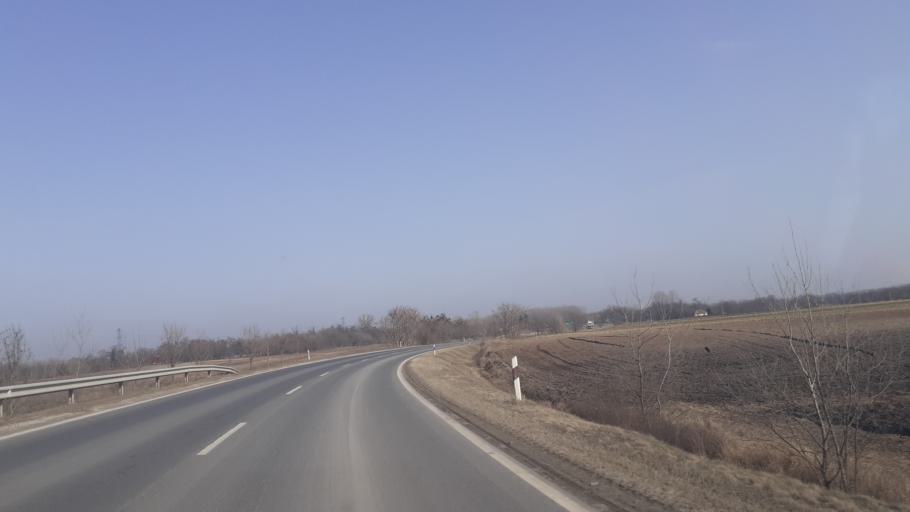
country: HU
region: Pest
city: Bugyi
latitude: 47.2407
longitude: 19.1226
